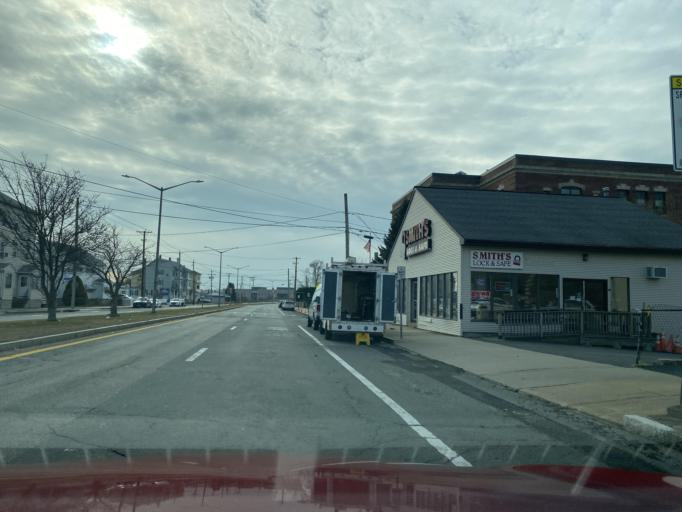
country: US
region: Massachusetts
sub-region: Bristol County
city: Fall River
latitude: 41.6851
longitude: -71.1302
